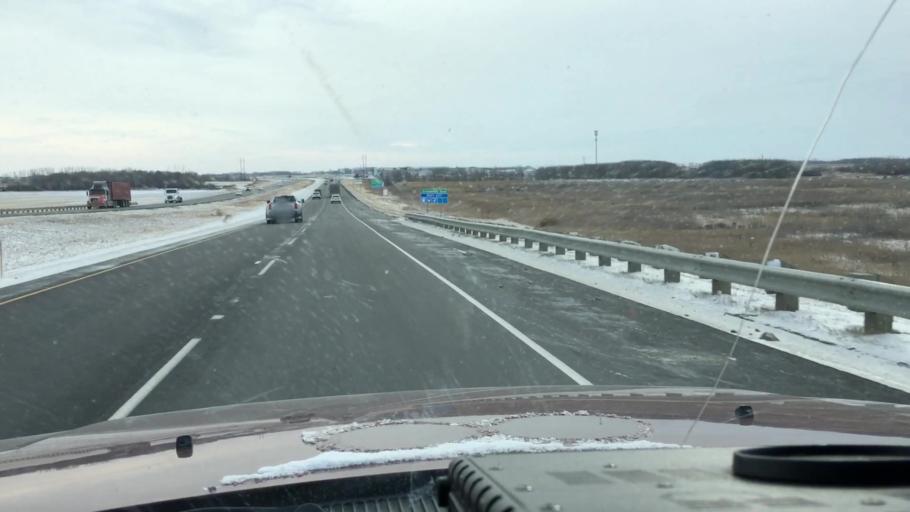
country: CA
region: Saskatchewan
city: Saskatoon
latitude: 52.0678
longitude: -106.6029
